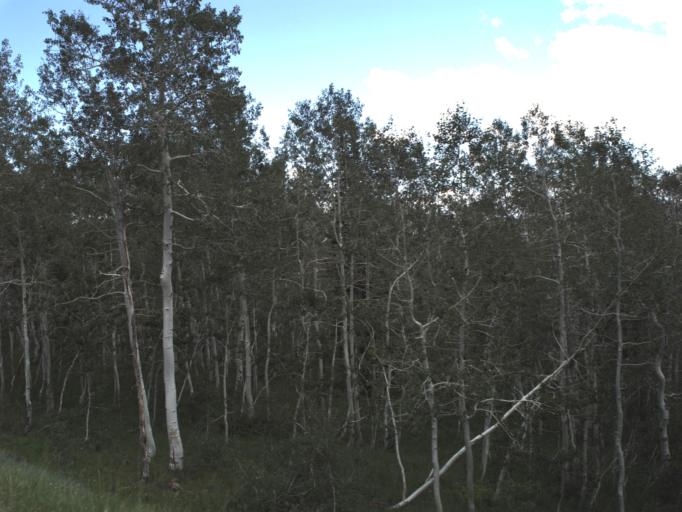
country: US
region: Utah
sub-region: Weber County
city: Wolf Creek
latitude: 41.4489
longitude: -111.5020
